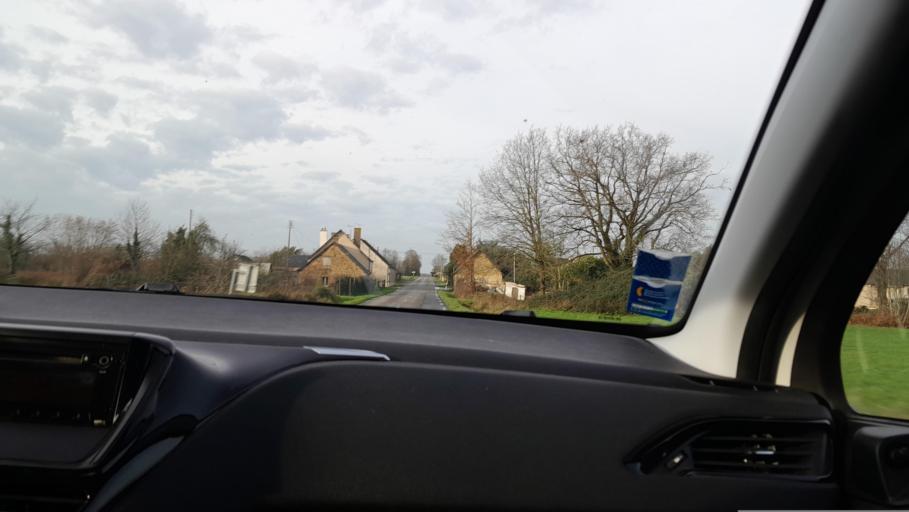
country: FR
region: Brittany
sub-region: Departement d'Ille-et-Vilaine
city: La Guerche-de-Bretagne
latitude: 47.9016
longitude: -1.1424
